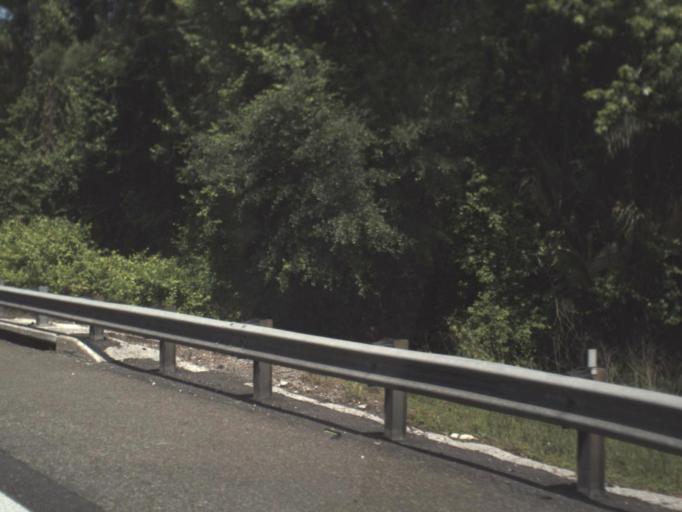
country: US
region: Florida
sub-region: Duval County
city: Baldwin
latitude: 30.3050
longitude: -81.8954
